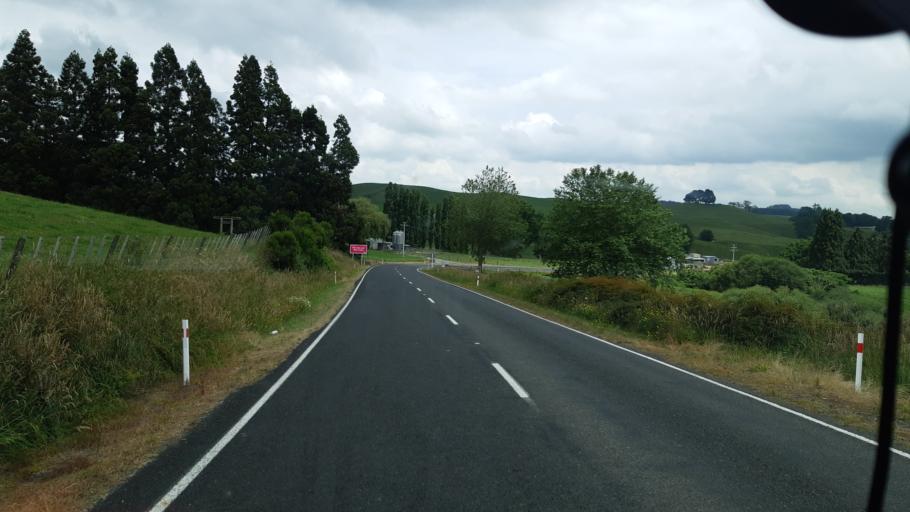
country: NZ
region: Waikato
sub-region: Waipa District
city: Cambridge
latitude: -38.1407
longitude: 175.5345
